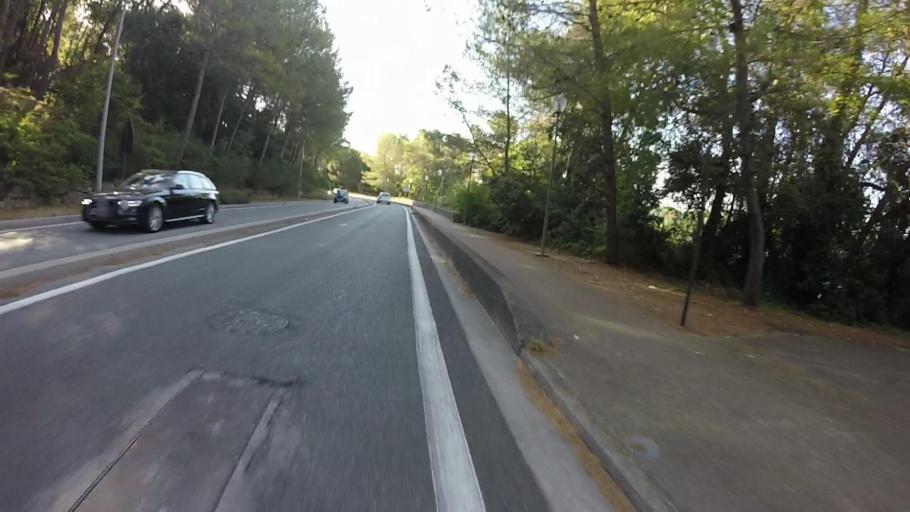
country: FR
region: Provence-Alpes-Cote d'Azur
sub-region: Departement des Alpes-Maritimes
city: Mougins
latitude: 43.6107
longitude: 7.0188
